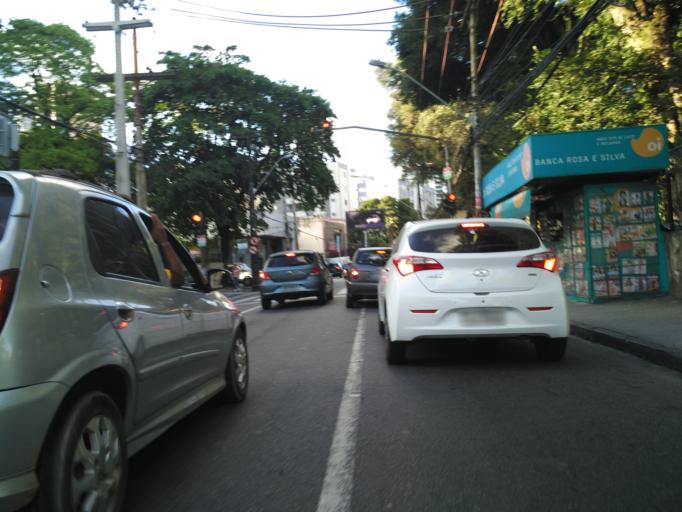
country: BR
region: Pernambuco
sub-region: Recife
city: Recife
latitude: -8.0484
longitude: -34.8967
